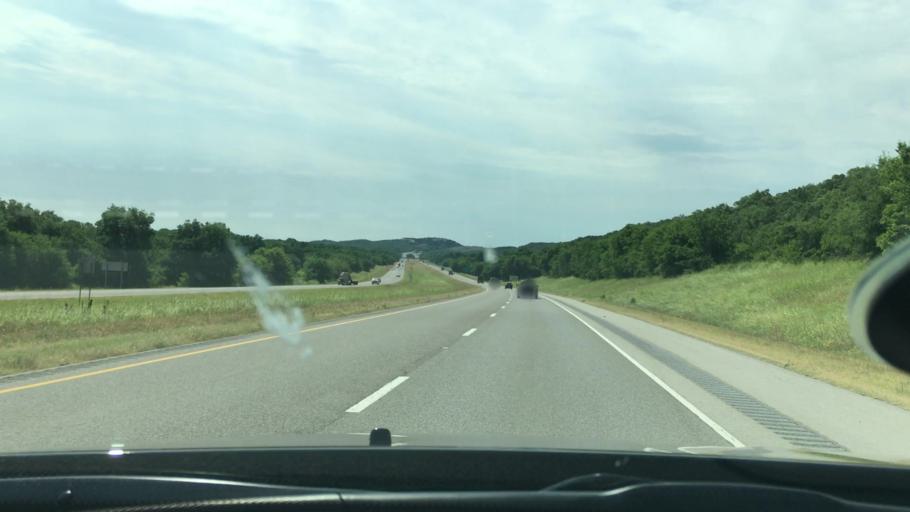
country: US
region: Oklahoma
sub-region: Murray County
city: Davis
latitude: 34.4698
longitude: -97.1535
